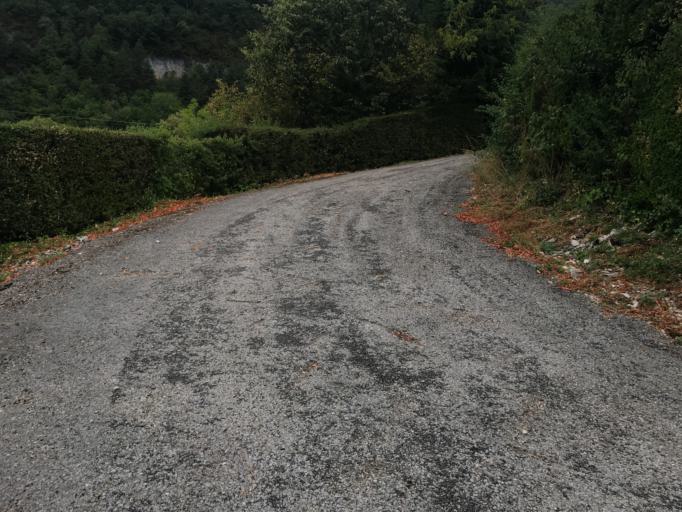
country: FR
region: Rhone-Alpes
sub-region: Departement de l'Ain
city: Dortan
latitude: 46.3377
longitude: 5.6238
